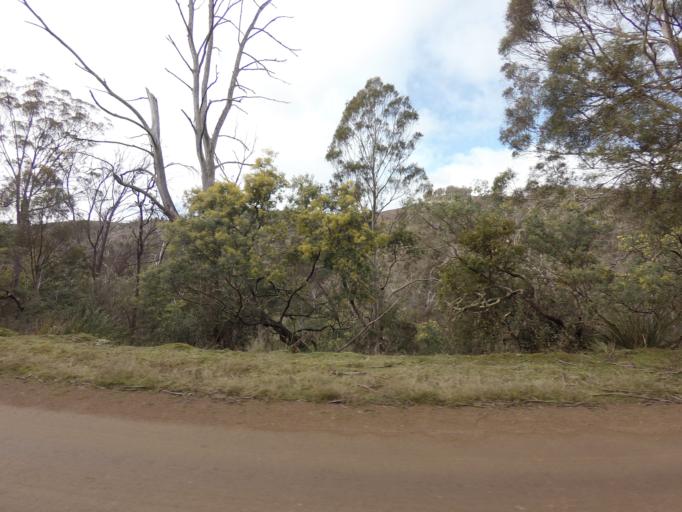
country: AU
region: Tasmania
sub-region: Derwent Valley
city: New Norfolk
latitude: -42.7399
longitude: 146.8690
